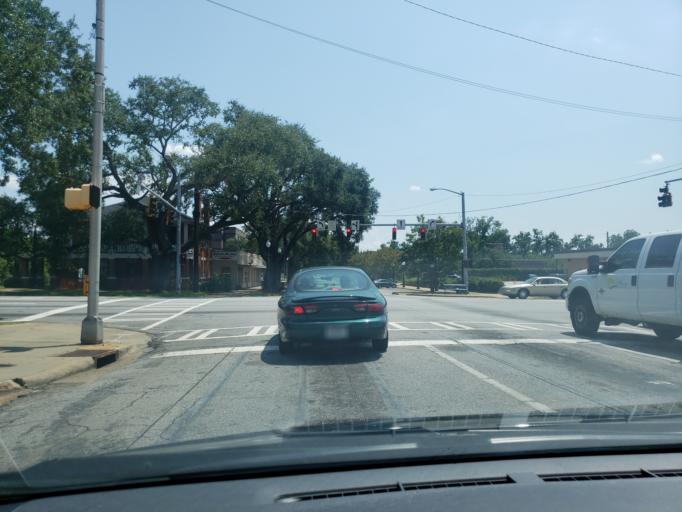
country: US
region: Georgia
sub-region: Dougherty County
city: Albany
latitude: 31.5756
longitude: -84.1536
